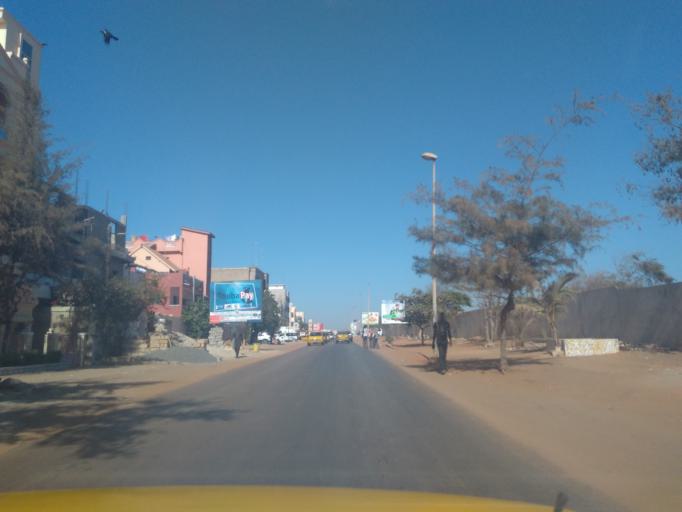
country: SN
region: Dakar
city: Grand Dakar
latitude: 14.7596
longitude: -17.4574
